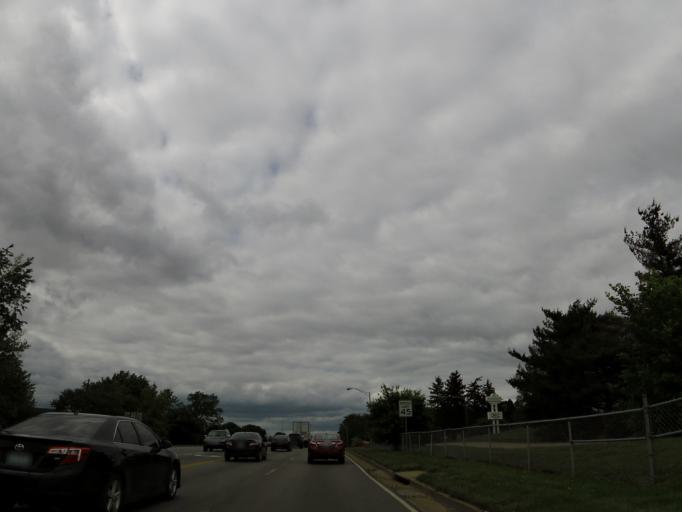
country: US
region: Kentucky
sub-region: Scott County
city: Georgetown
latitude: 38.2153
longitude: -84.5404
